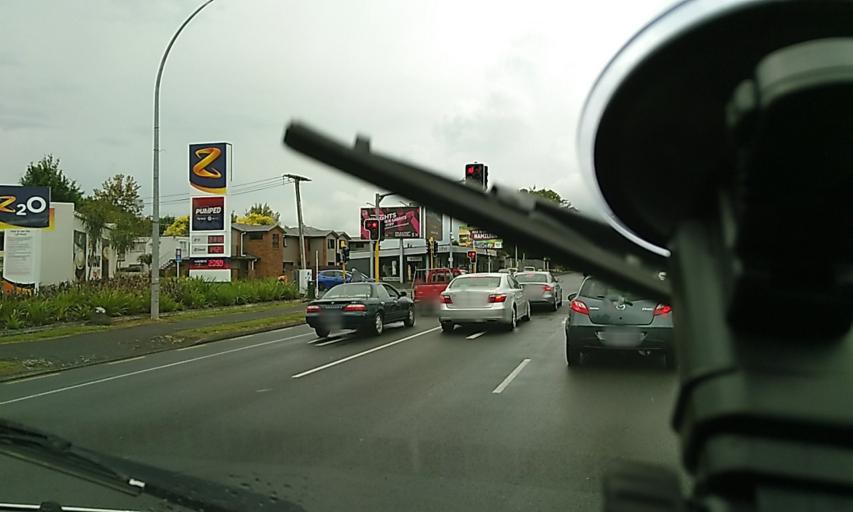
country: NZ
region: Waikato
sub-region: Hamilton City
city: Hamilton
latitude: -37.7808
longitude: 175.2716
